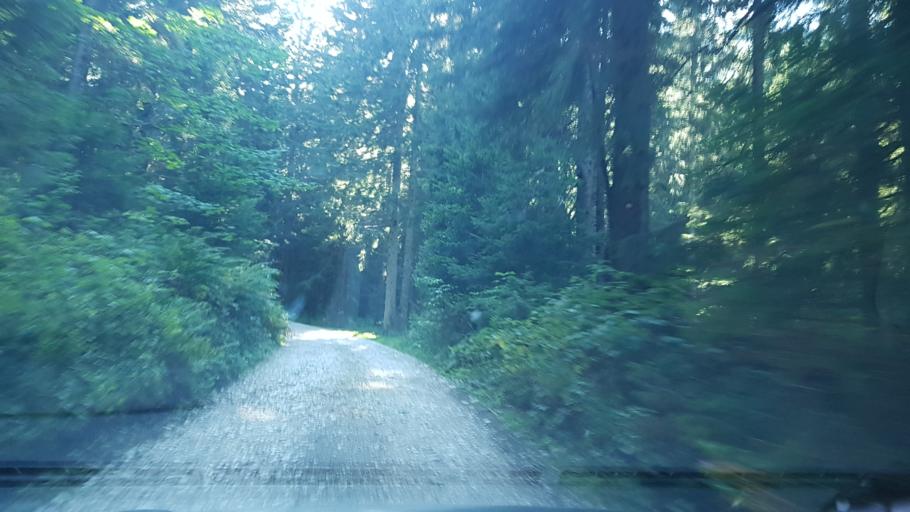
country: SI
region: Ravne na Koroskem
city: Kotlje
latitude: 46.4848
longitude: 14.9757
